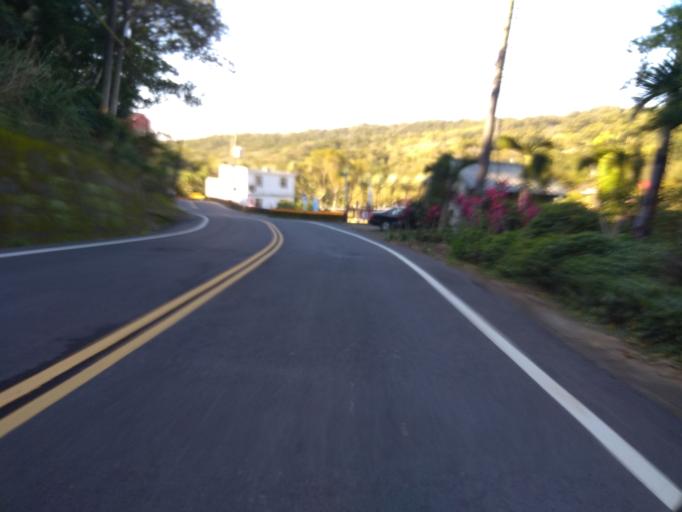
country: TW
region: Taiwan
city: Daxi
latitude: 24.8572
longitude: 121.1508
